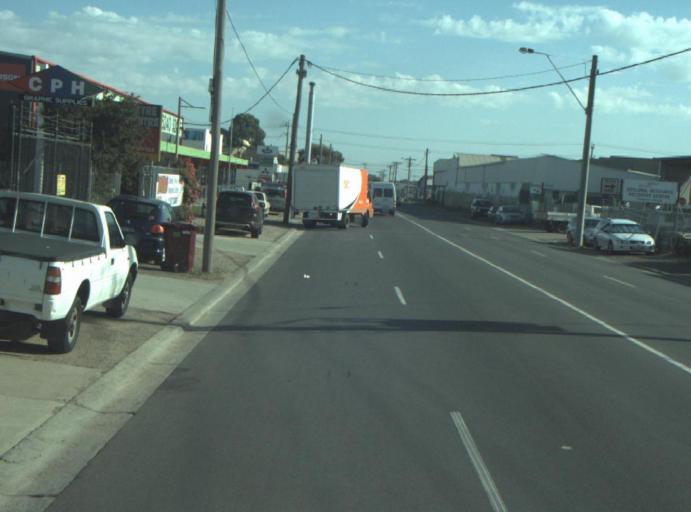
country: AU
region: Victoria
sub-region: Greater Geelong
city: Bell Park
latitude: -38.1160
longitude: 144.3489
